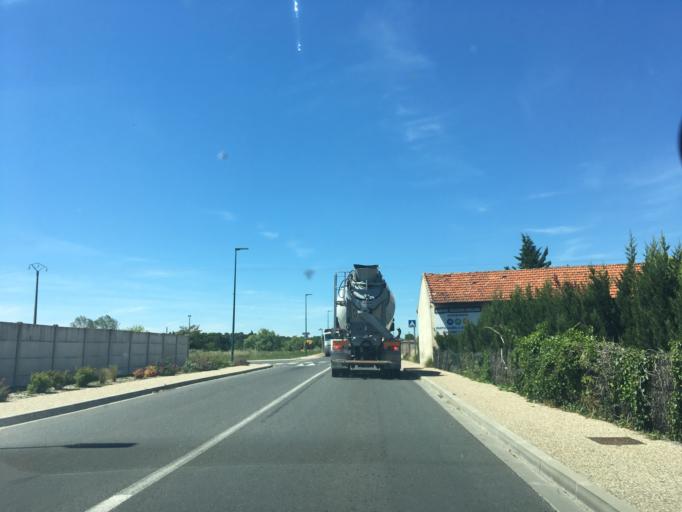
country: FR
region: Aquitaine
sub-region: Departement de la Gironde
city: Listrac-Medoc
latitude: 45.0758
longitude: -0.7928
